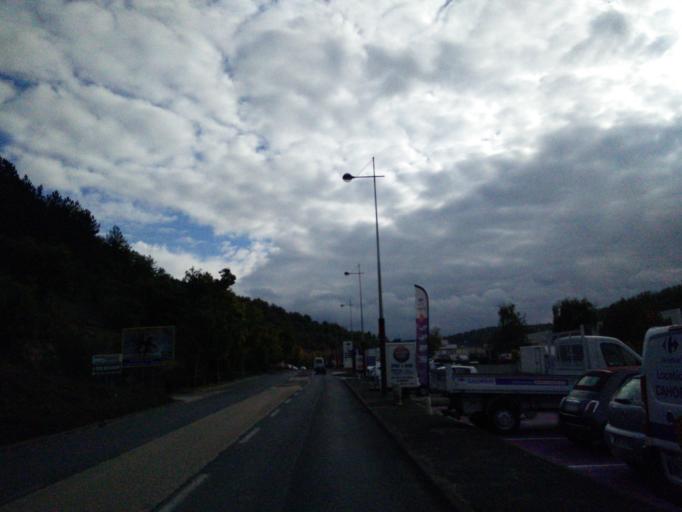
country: FR
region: Midi-Pyrenees
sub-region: Departement du Lot
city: Cahors
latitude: 44.4213
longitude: 1.4392
